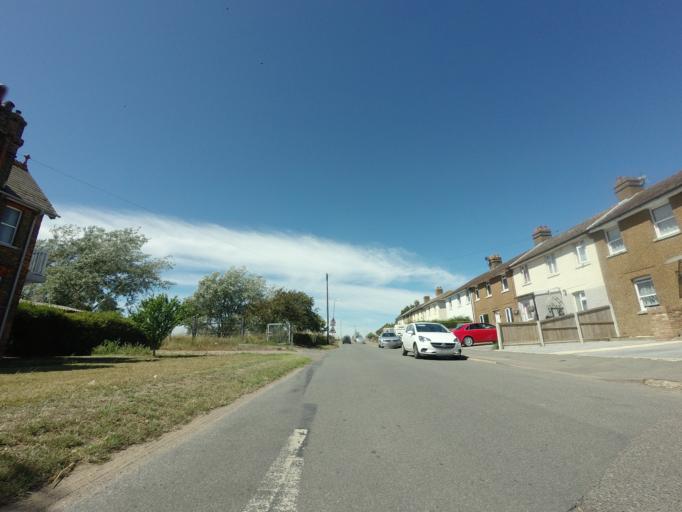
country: GB
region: England
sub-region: Kent
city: Deal
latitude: 51.2364
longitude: 1.3983
